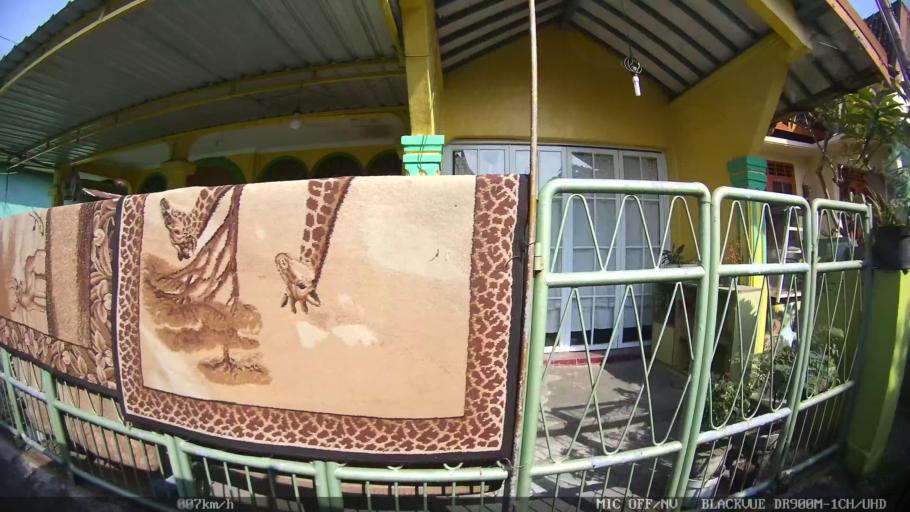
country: ID
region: Daerah Istimewa Yogyakarta
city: Yogyakarta
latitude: -7.7857
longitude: 110.3539
